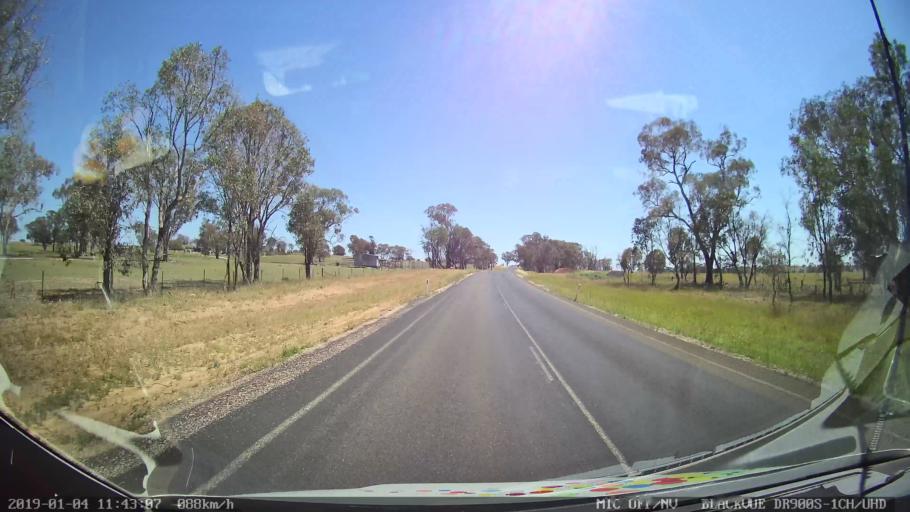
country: AU
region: New South Wales
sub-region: Cabonne
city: Molong
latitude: -32.9730
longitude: 148.7844
